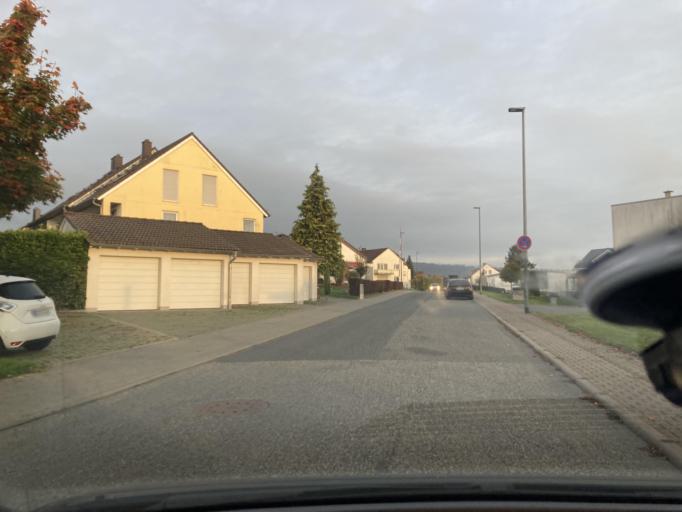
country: DE
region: Hesse
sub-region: Regierungsbezirk Darmstadt
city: Oberursel
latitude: 50.2217
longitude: 8.5784
